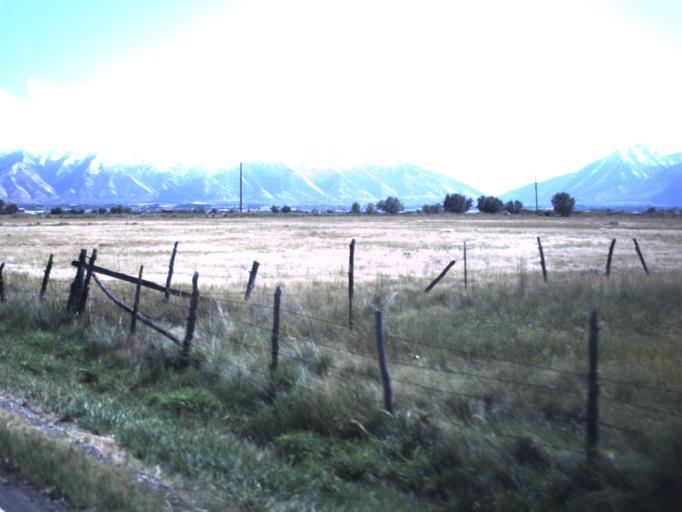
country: US
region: Utah
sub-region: Utah County
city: Spanish Fork
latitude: 40.1585
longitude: -111.6837
